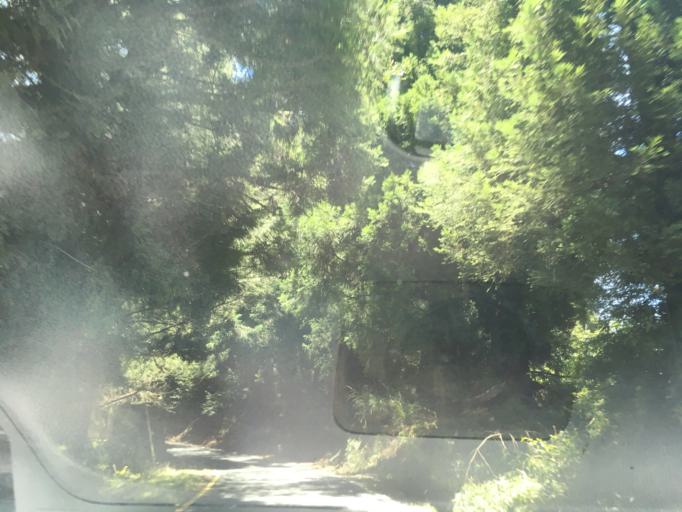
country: TW
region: Taiwan
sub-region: Nantou
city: Puli
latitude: 24.2338
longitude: 121.2423
